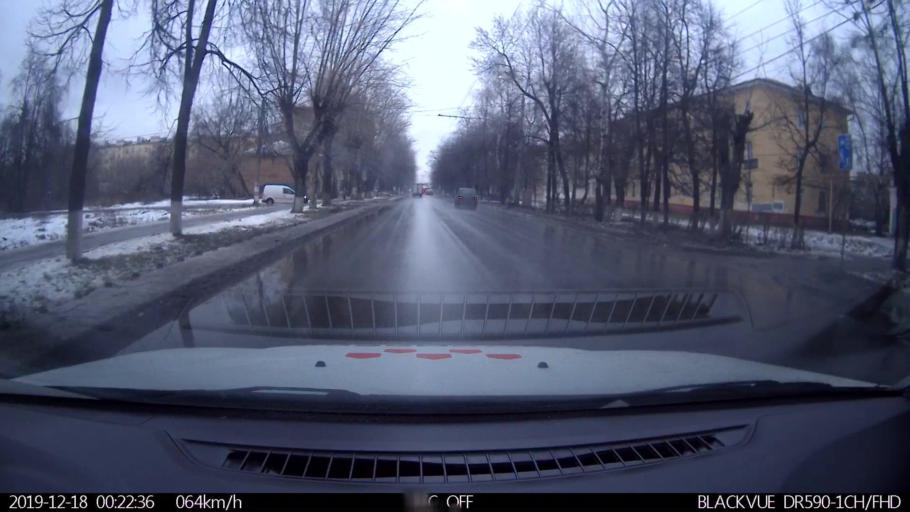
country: RU
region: Nizjnij Novgorod
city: Nizhniy Novgorod
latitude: 56.3334
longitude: 43.8853
